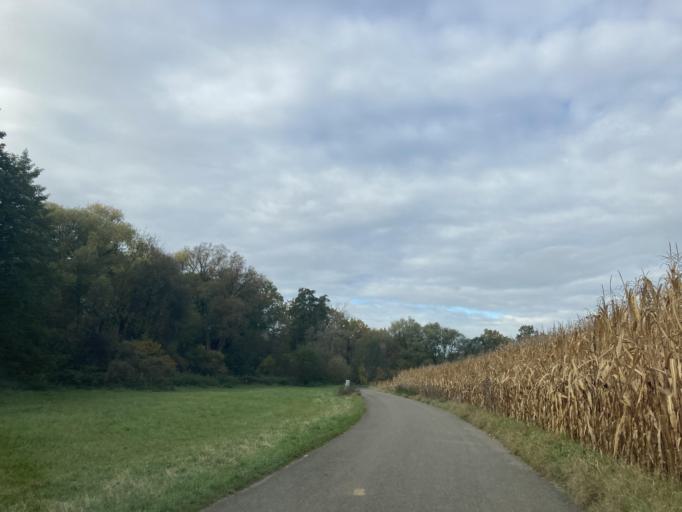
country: DE
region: Baden-Wuerttemberg
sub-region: Tuebingen Region
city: Gomaringen
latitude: 48.4509
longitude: 9.0790
